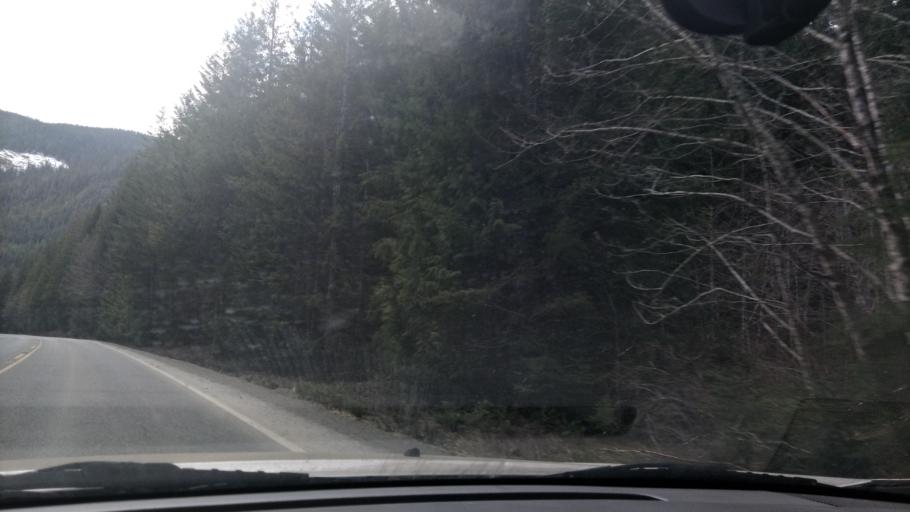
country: CA
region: British Columbia
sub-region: Regional District of Alberni-Clayoquot
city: Tofino
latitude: 49.8287
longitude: -125.9716
